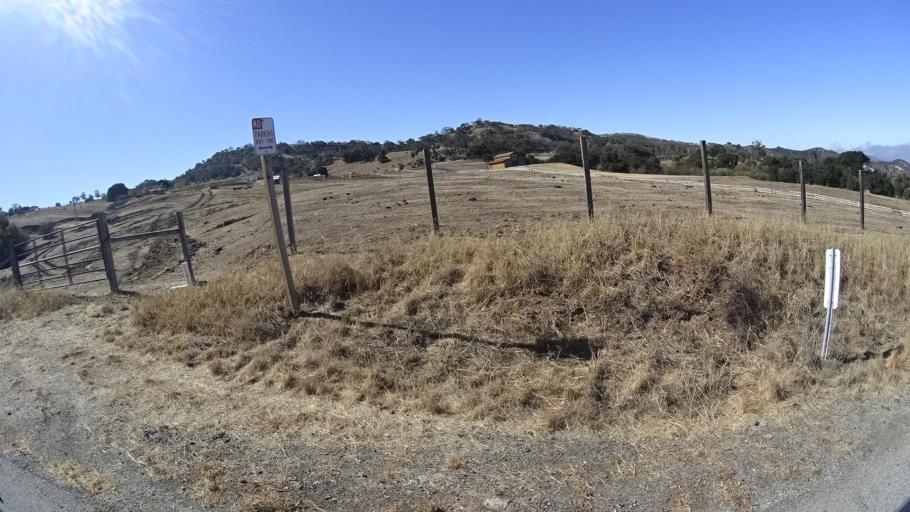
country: US
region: California
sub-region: Monterey County
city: Carmel Valley Village
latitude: 36.5508
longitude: -121.6728
